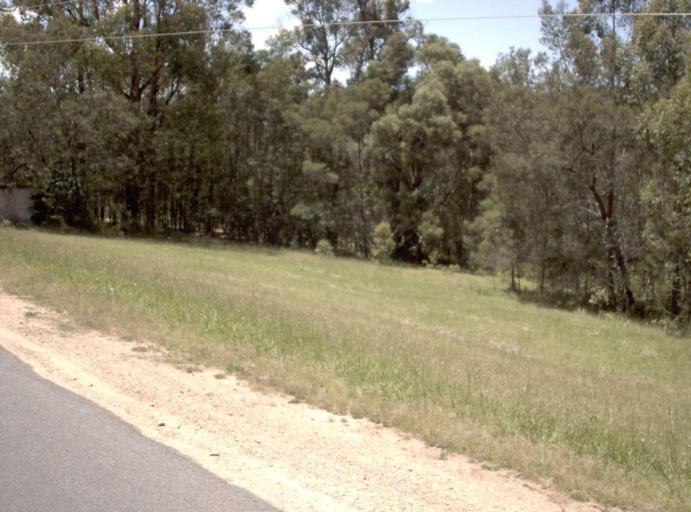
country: AU
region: New South Wales
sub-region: Bombala
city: Bombala
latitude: -37.5494
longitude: 148.9371
